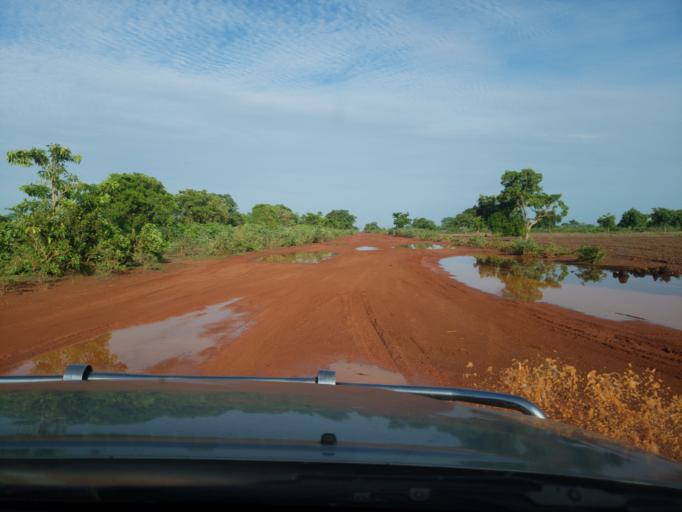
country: ML
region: Sikasso
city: Koutiala
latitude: 12.4278
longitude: -5.6297
